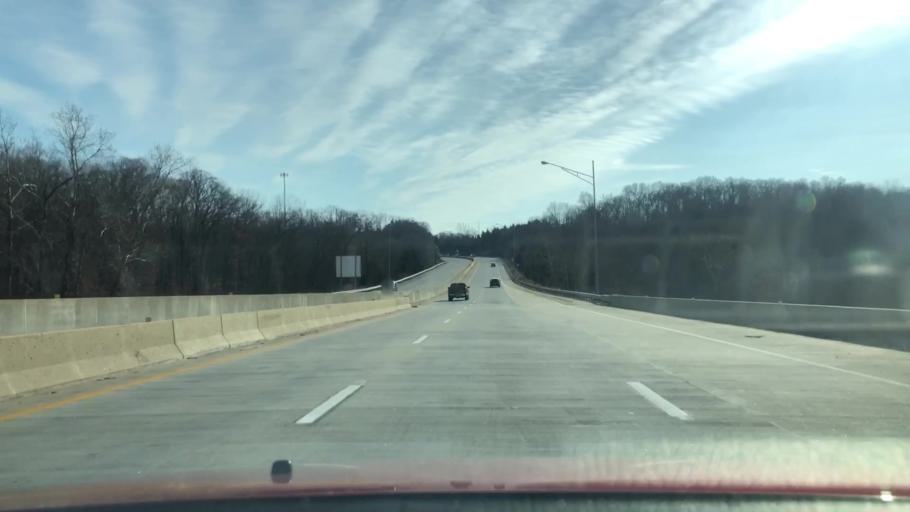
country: US
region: Missouri
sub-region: Christian County
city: Ozark
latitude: 37.1245
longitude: -93.2262
